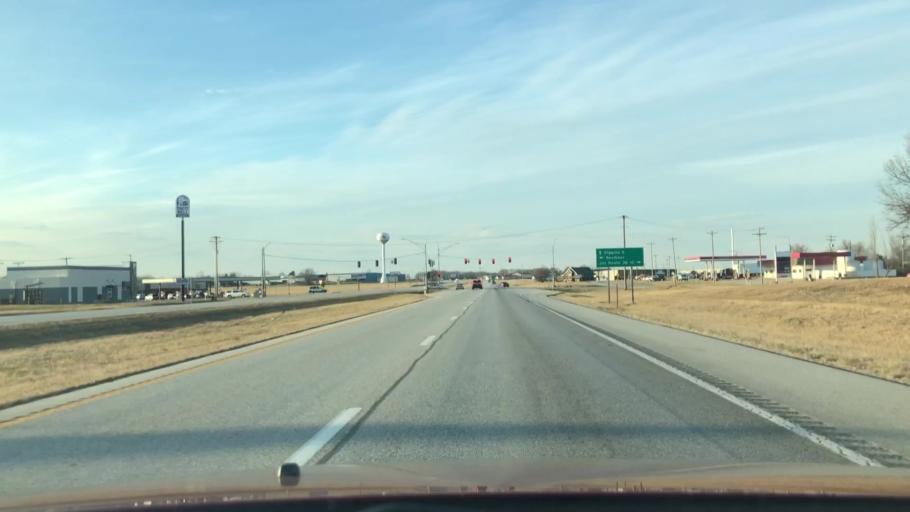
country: US
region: Missouri
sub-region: Webster County
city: Seymour
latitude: 37.1487
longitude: -92.7520
